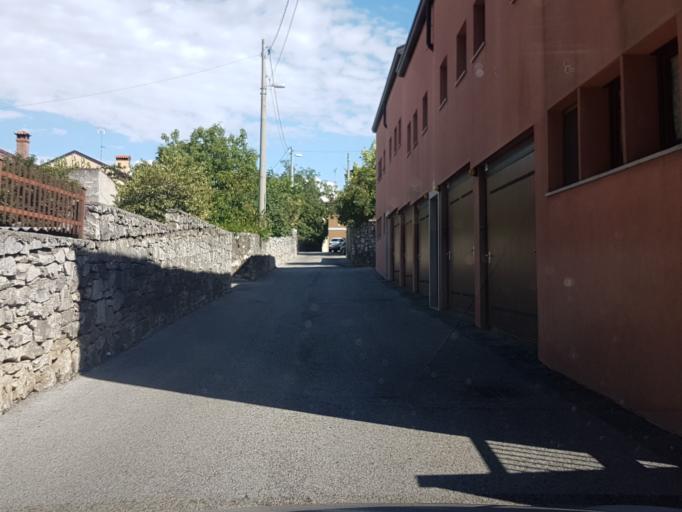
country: IT
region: Friuli Venezia Giulia
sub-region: Provincia di Trieste
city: Santa Croce
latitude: 45.7349
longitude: 13.6913
